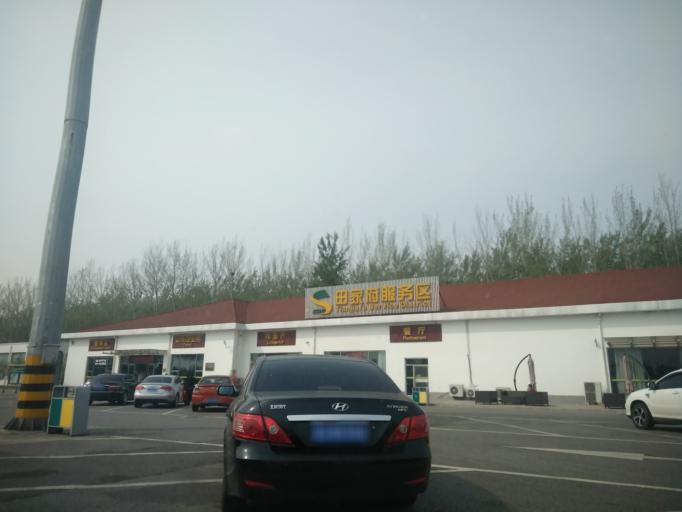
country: CN
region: Beijing
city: Taihu
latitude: 39.8403
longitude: 116.6644
